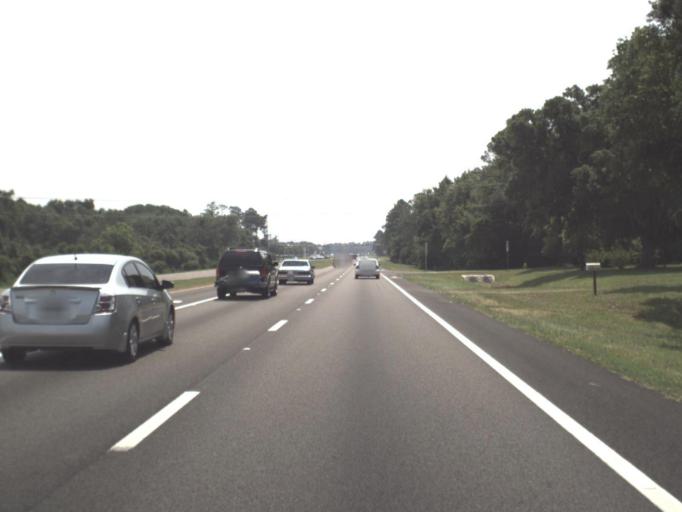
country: US
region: Florida
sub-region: Nassau County
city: Fernandina Beach
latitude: 30.6200
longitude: -81.5247
